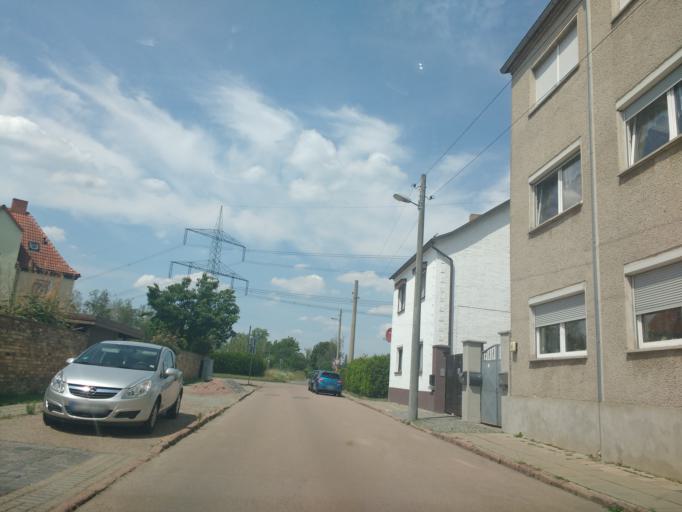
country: DE
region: Saxony-Anhalt
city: Dieskau
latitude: 51.4583
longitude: 12.0335
